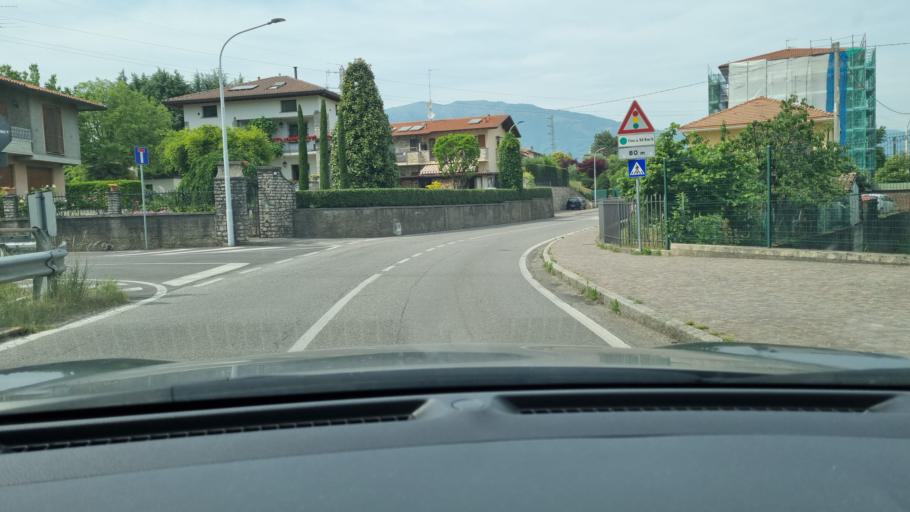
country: IT
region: Lombardy
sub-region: Provincia di Bergamo
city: Mapello
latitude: 45.7125
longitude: 9.5478
